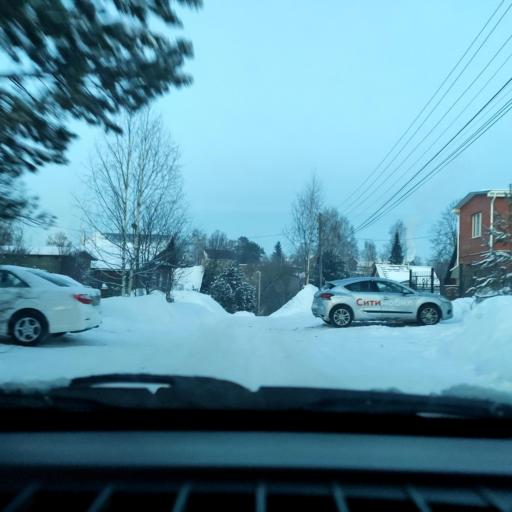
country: RU
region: Perm
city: Perm
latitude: 58.0420
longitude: 56.3383
